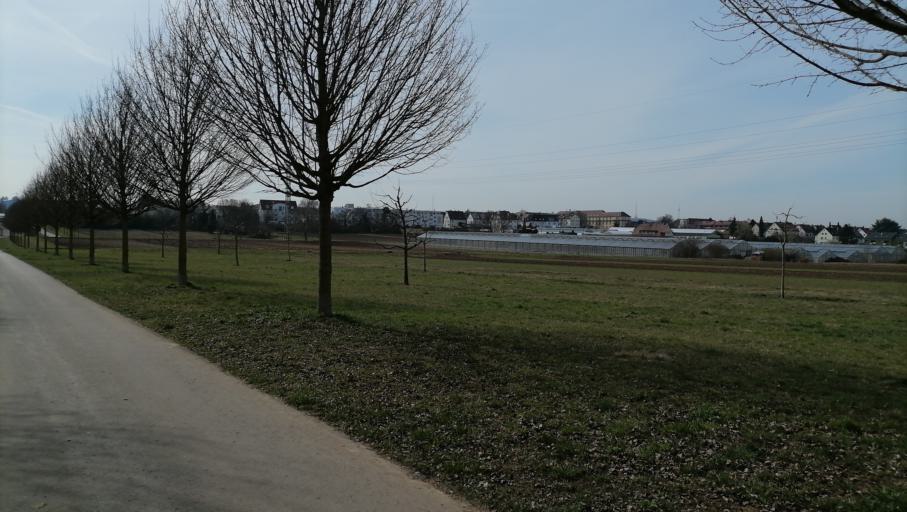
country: DE
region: Baden-Wuerttemberg
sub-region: Regierungsbezirk Stuttgart
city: Fellbach
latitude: 48.8141
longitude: 9.2570
